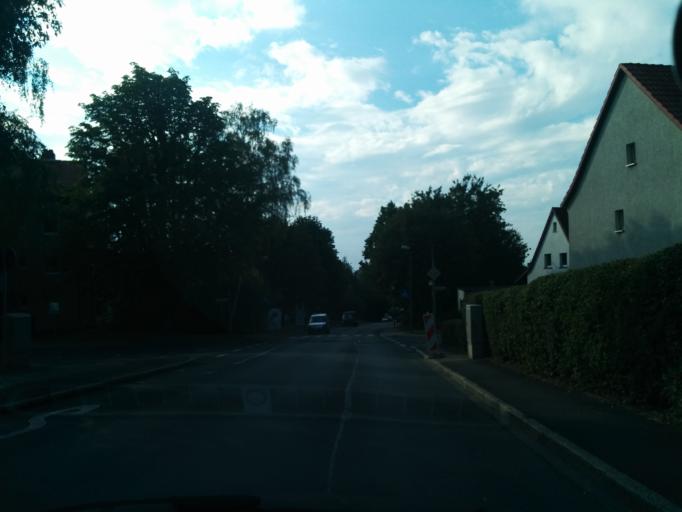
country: DE
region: Lower Saxony
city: Goettingen
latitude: 51.5232
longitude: 9.9617
